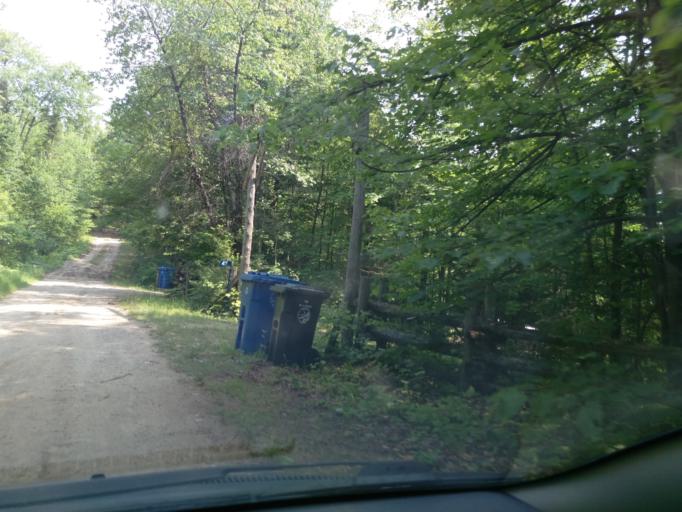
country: CA
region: Quebec
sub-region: Outaouais
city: Maniwaki
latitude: 46.2008
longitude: -76.1428
